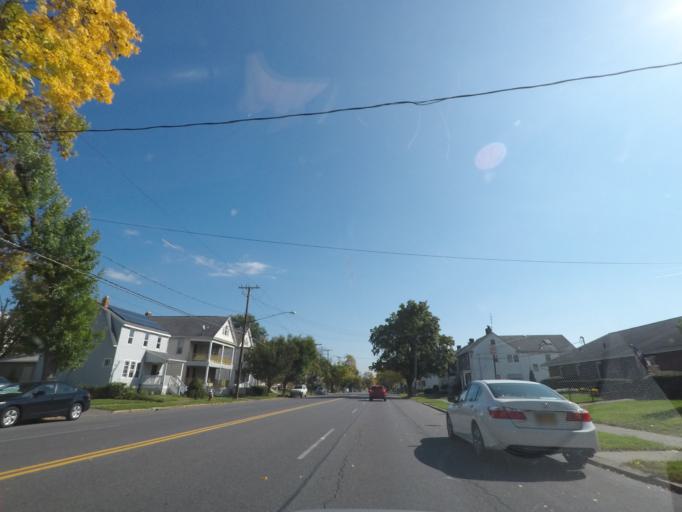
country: US
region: New York
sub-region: Albany County
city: West Albany
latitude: 42.6704
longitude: -73.7869
